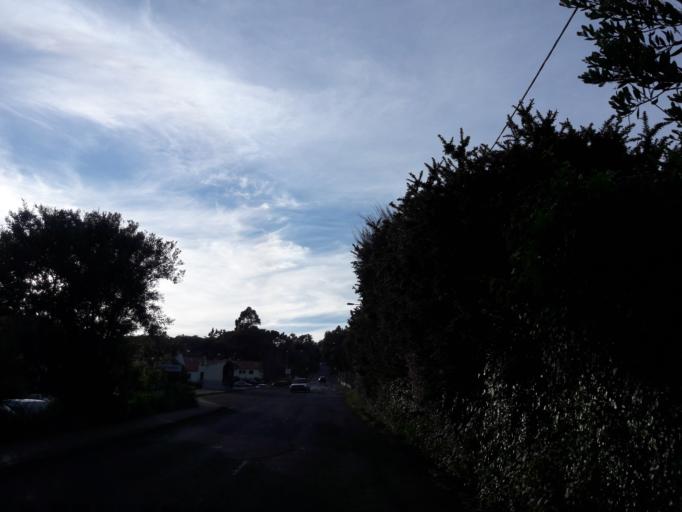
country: PT
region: Madeira
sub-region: Santa Cruz
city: Camacha
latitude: 32.6713
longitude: -16.8473
